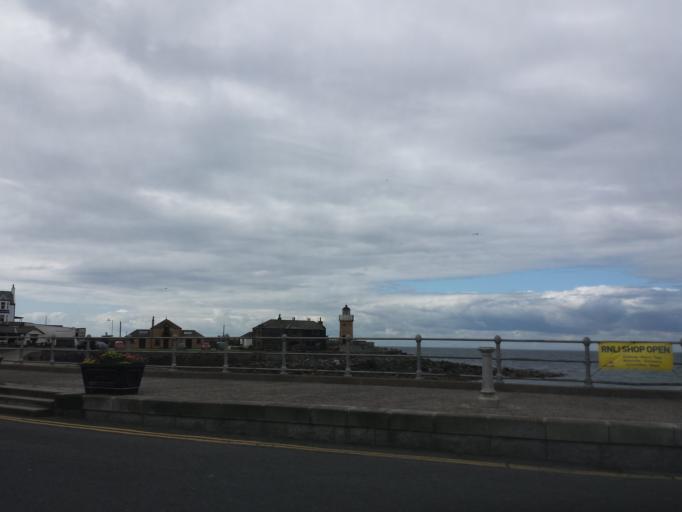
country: GB
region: Scotland
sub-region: Dumfries and Galloway
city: Stranraer
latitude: 54.8418
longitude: -5.1167
